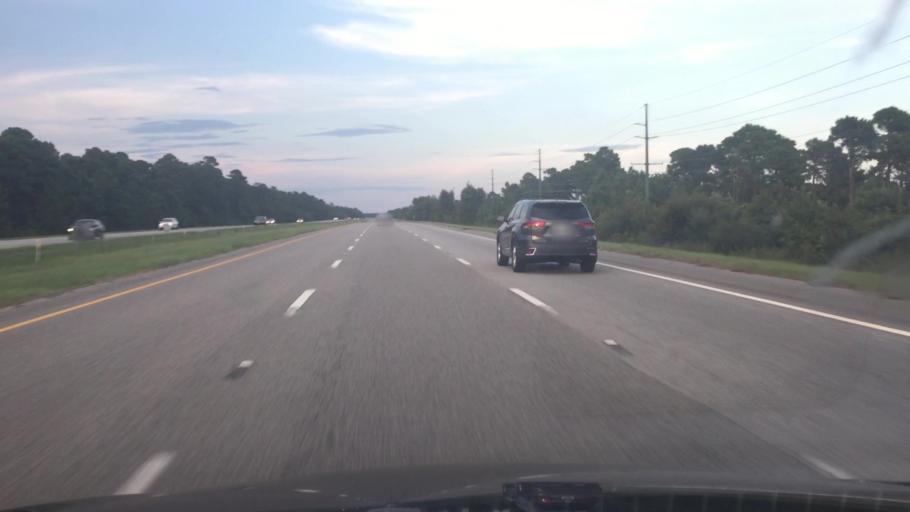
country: US
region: South Carolina
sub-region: Horry County
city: Forestbrook
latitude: 33.7436
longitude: -78.9263
